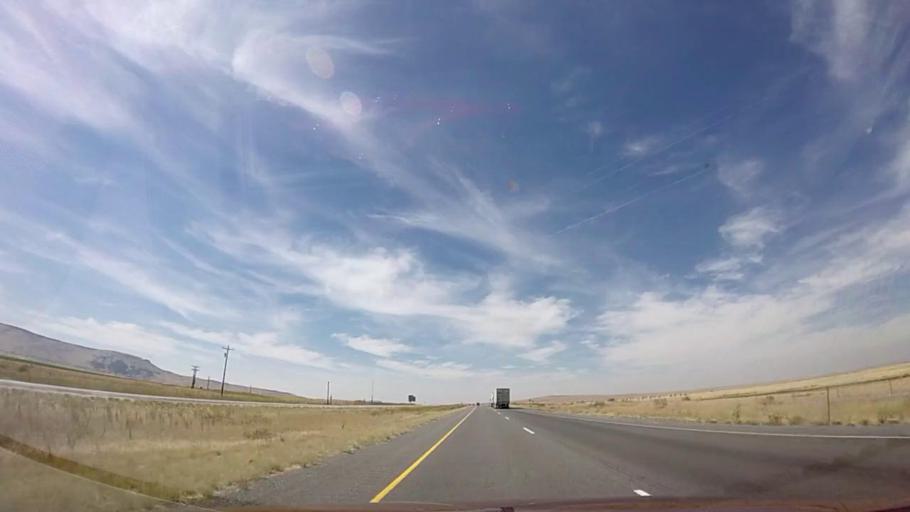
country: US
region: Idaho
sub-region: Minidoka County
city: Rupert
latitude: 42.5169
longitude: -113.4240
